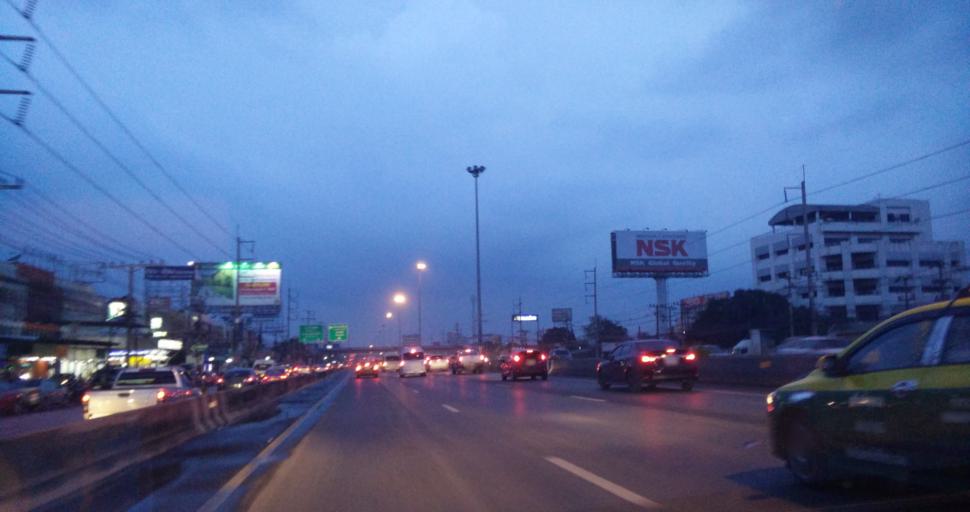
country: TH
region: Pathum Thani
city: Khlong Luang
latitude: 14.0274
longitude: 100.6157
